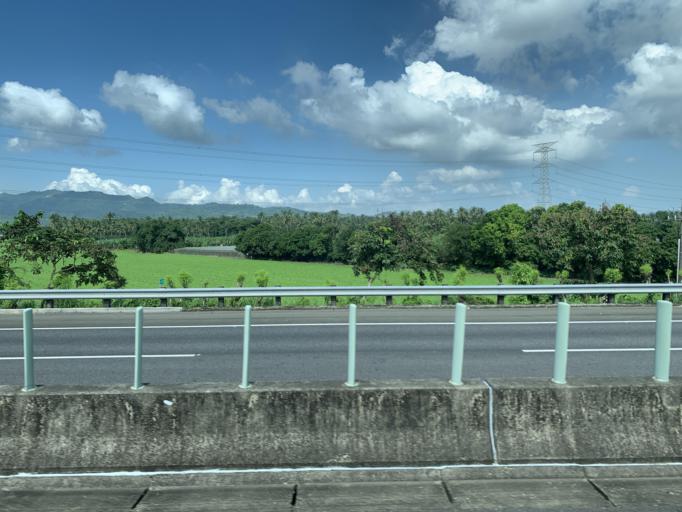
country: TW
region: Taiwan
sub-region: Pingtung
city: Pingtung
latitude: 22.8331
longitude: 120.4924
